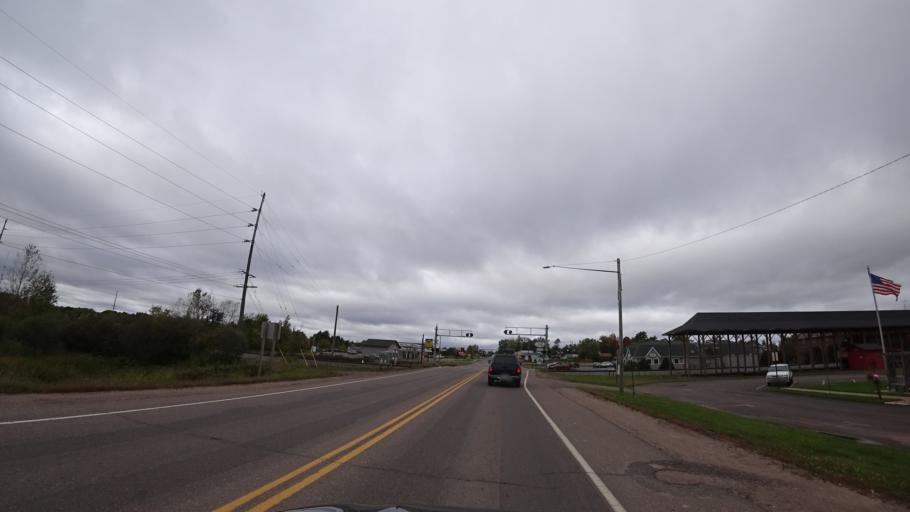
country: US
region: Wisconsin
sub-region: Rusk County
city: Ladysmith
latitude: 45.4626
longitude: -91.1110
